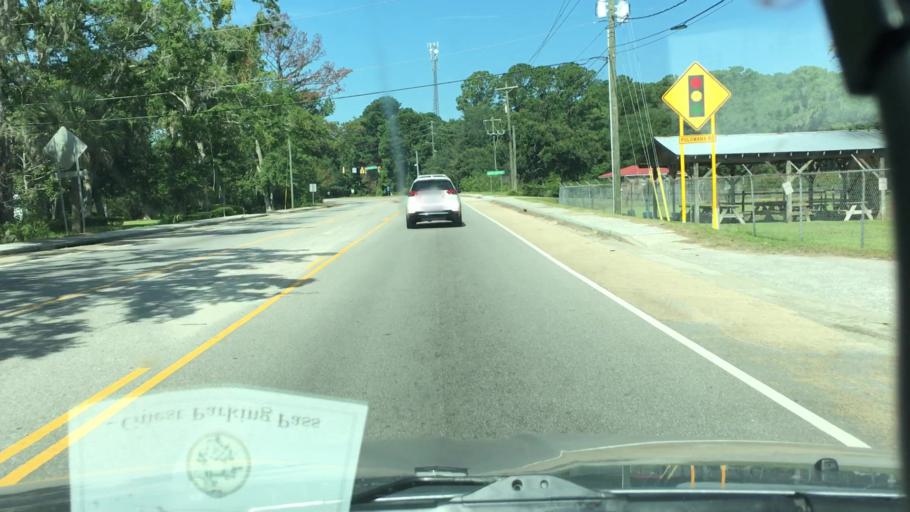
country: US
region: South Carolina
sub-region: Beaufort County
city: Beaufort
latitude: 32.3968
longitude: -80.5787
